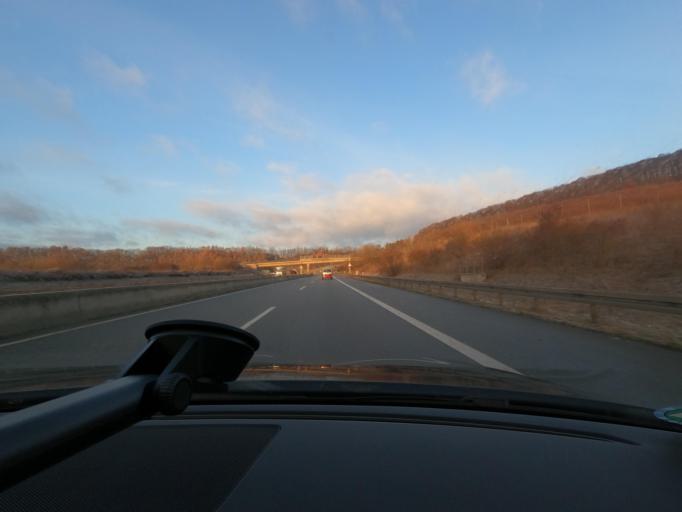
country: DE
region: Thuringia
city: Rustenfelde
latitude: 51.4036
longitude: 10.0121
